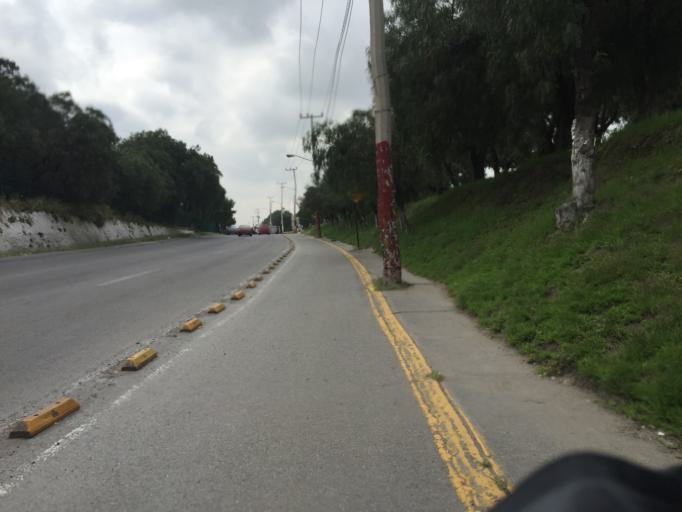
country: MX
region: Mexico
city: Cuautitlan Izcalli
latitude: 19.6578
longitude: -99.2069
